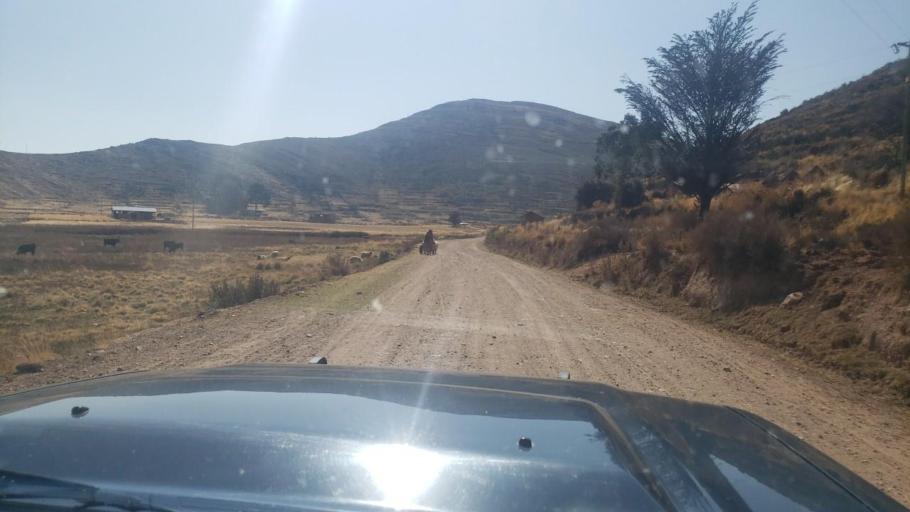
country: BO
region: La Paz
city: Huatajata
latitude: -16.3376
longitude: -68.6771
